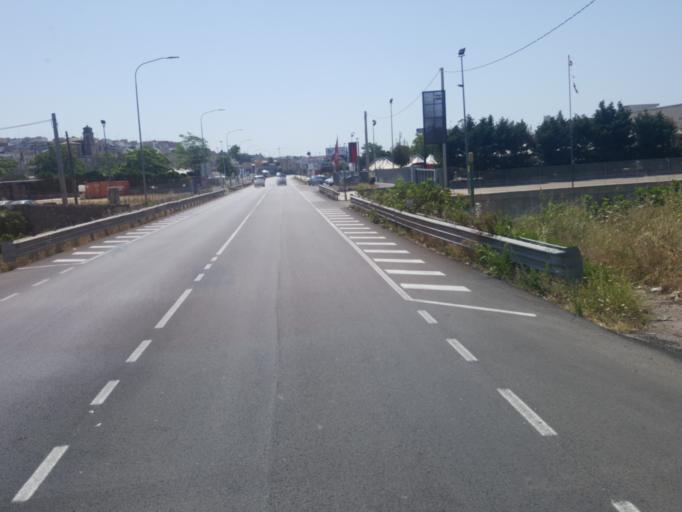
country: IT
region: Apulia
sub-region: Provincia di Taranto
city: Massafra
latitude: 40.5878
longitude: 17.1040
